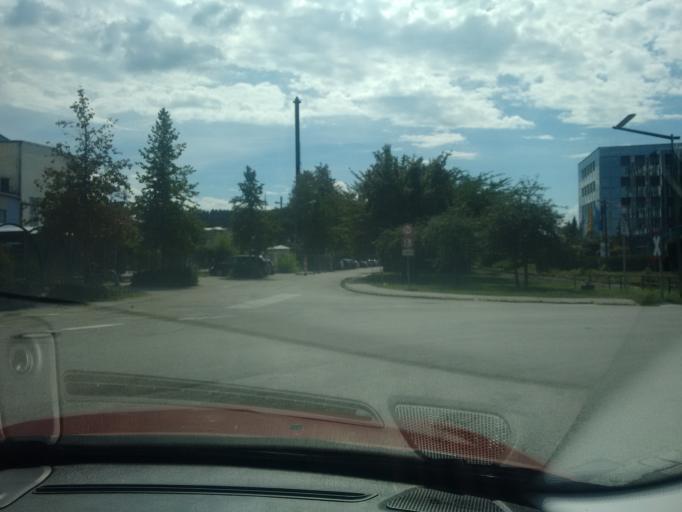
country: DE
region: Bavaria
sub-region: Upper Bavaria
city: Trostberg an der Alz
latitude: 48.0205
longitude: 12.5515
